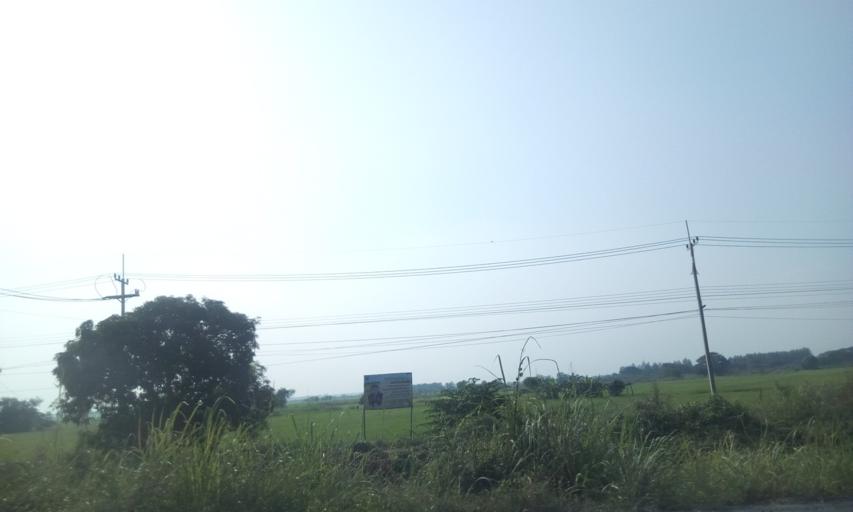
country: TH
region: Sing Buri
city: Phrom Buri
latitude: 14.7934
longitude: 100.4440
